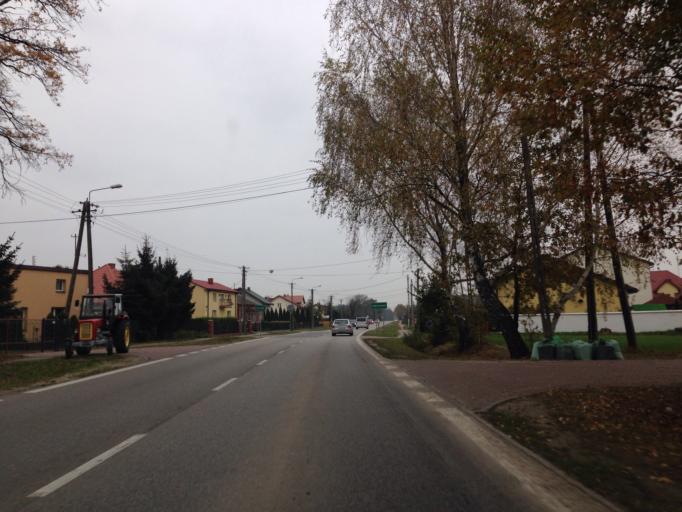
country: PL
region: Masovian Voivodeship
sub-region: Powiat warszawski zachodni
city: Leszno
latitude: 52.2615
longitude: 20.6232
